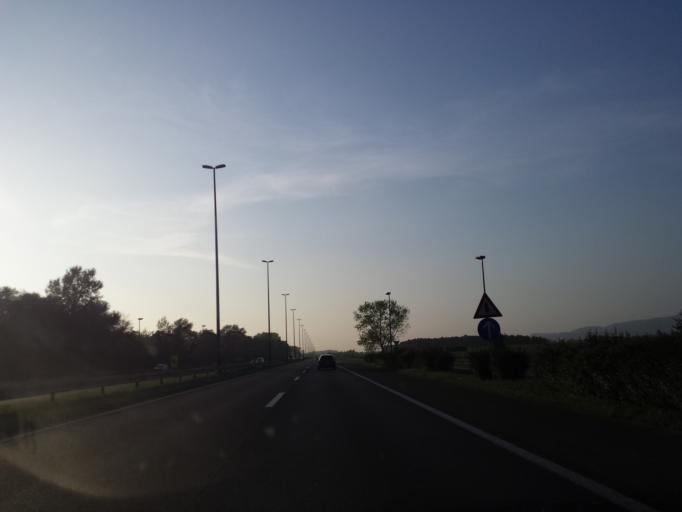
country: HR
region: Grad Zagreb
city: Lucko
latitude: 45.7754
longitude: 15.8780
